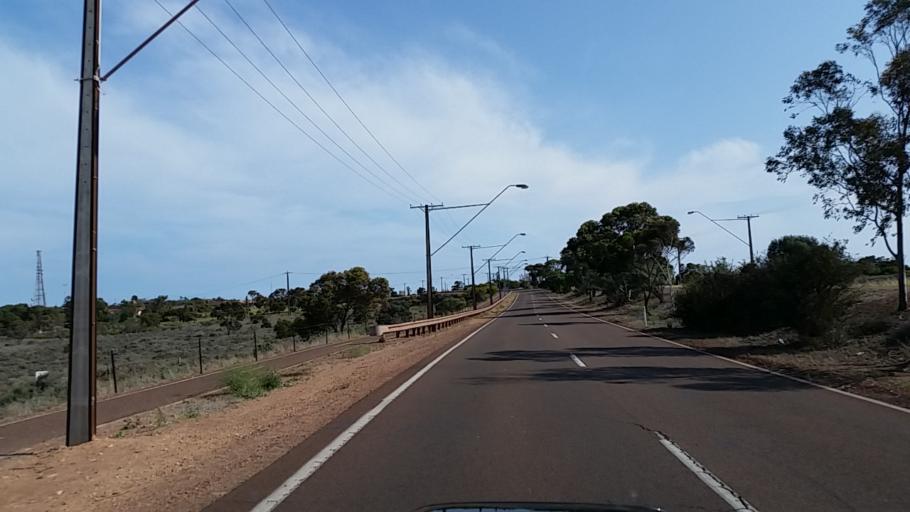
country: AU
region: South Australia
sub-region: Whyalla
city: Whyalla
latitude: -33.0212
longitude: 137.5742
